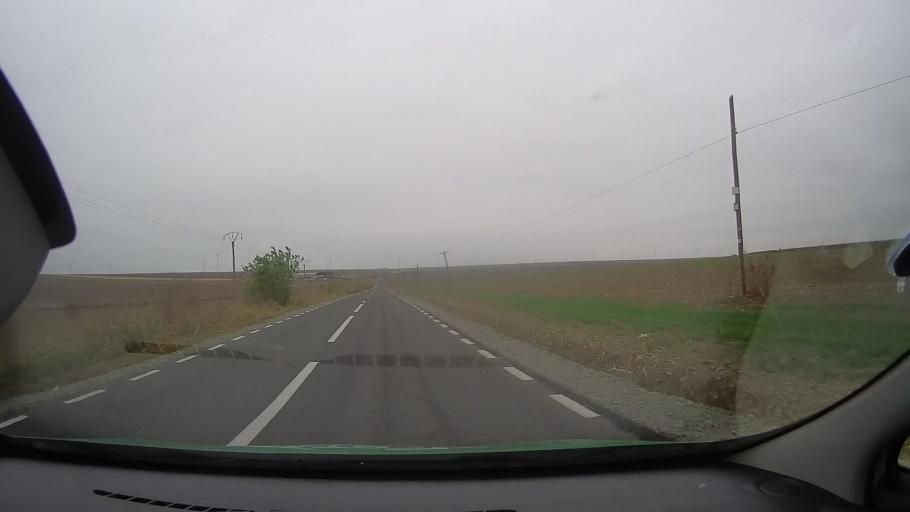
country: RO
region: Constanta
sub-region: Comuna Tortoman
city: Tortoman
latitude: 44.3580
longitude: 28.2112
